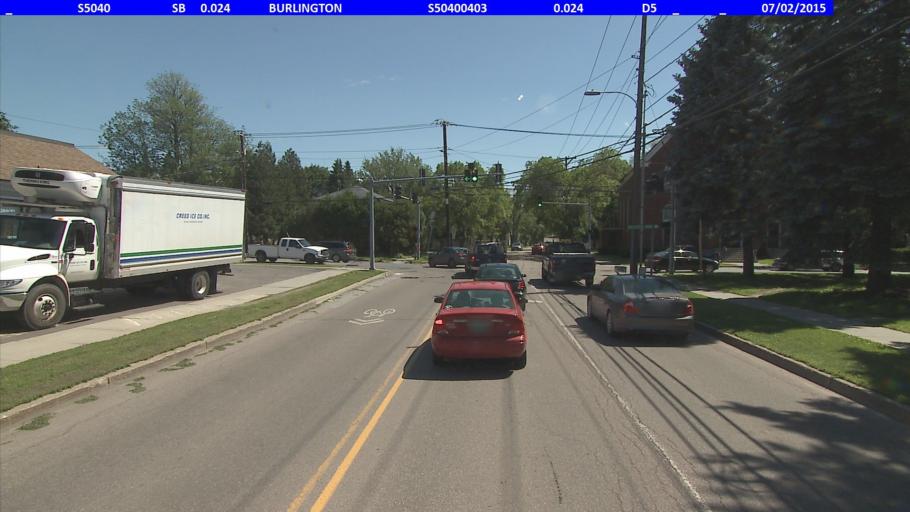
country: US
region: Vermont
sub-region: Chittenden County
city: Burlington
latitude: 44.4558
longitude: -73.2142
